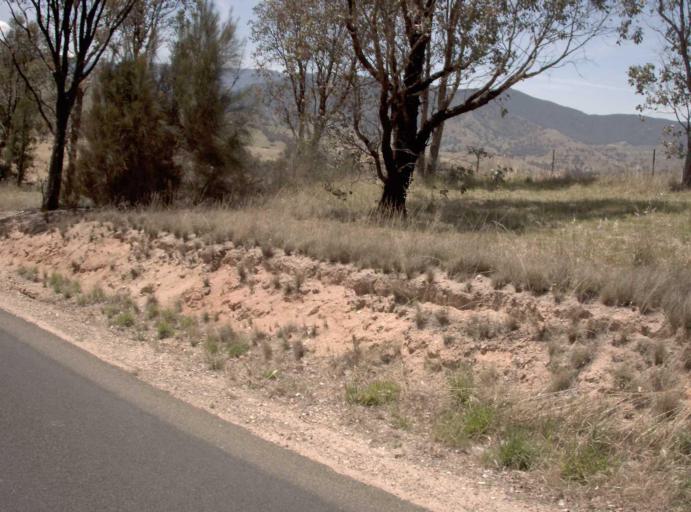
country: AU
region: Victoria
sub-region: East Gippsland
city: Bairnsdale
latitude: -37.1667
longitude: 147.6823
